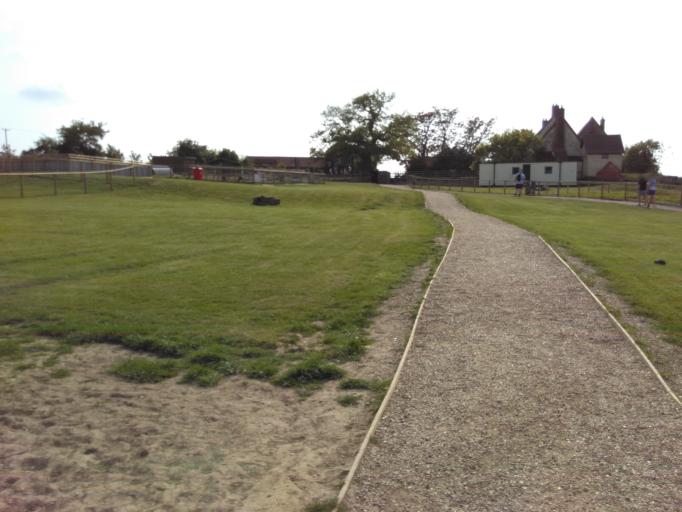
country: GB
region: England
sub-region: Suffolk
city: Ipswich
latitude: 52.0204
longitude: 1.1257
